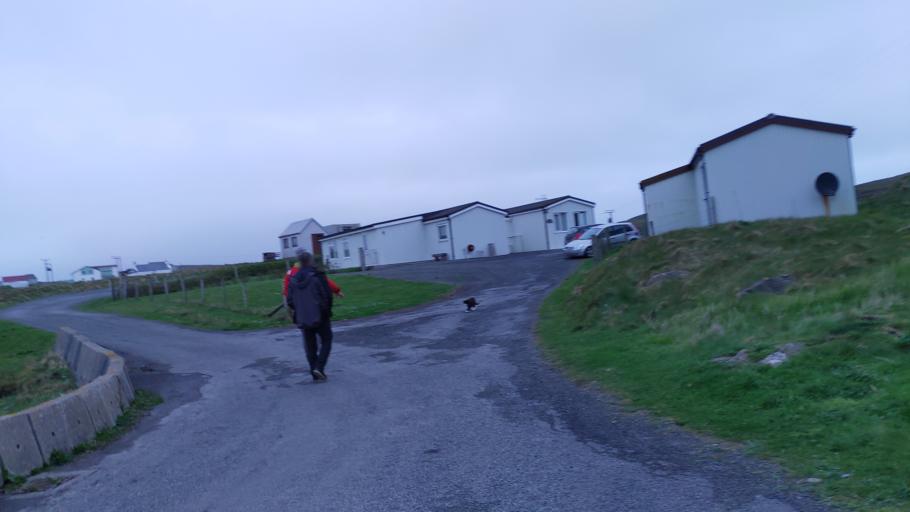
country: GB
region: Scotland
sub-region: Shetland Islands
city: Shetland
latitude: 60.4234
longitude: -0.7508
